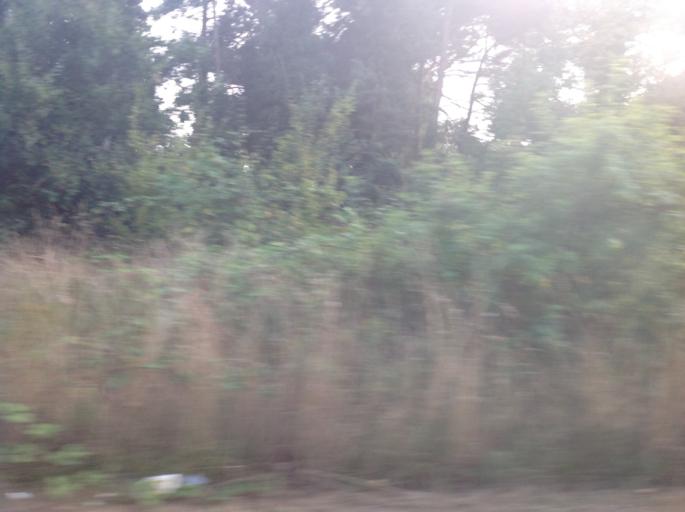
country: GB
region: England
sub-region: Suffolk
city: Felixstowe
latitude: 51.9731
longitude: 1.3450
